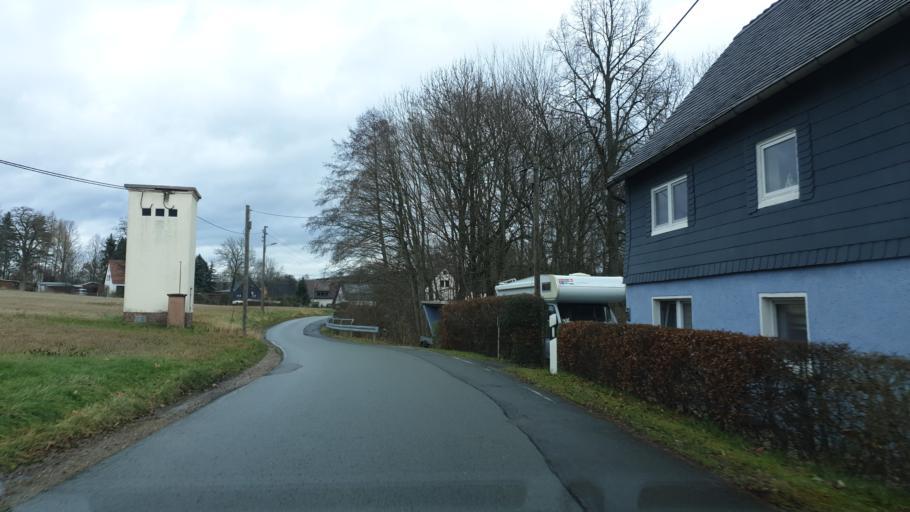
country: DE
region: Saxony
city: Bernsdorf
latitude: 50.7574
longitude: 12.6633
